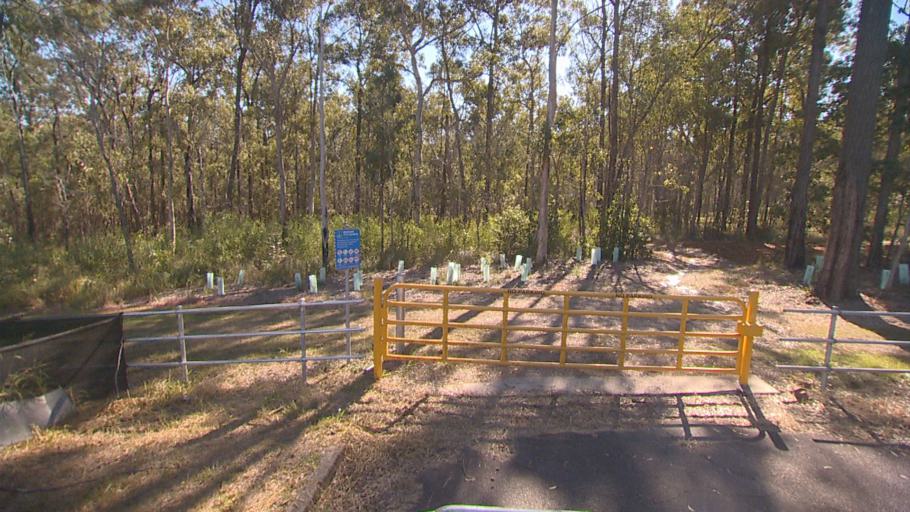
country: AU
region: Queensland
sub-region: Brisbane
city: Sunnybank Hills
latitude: -27.6552
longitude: 153.0462
